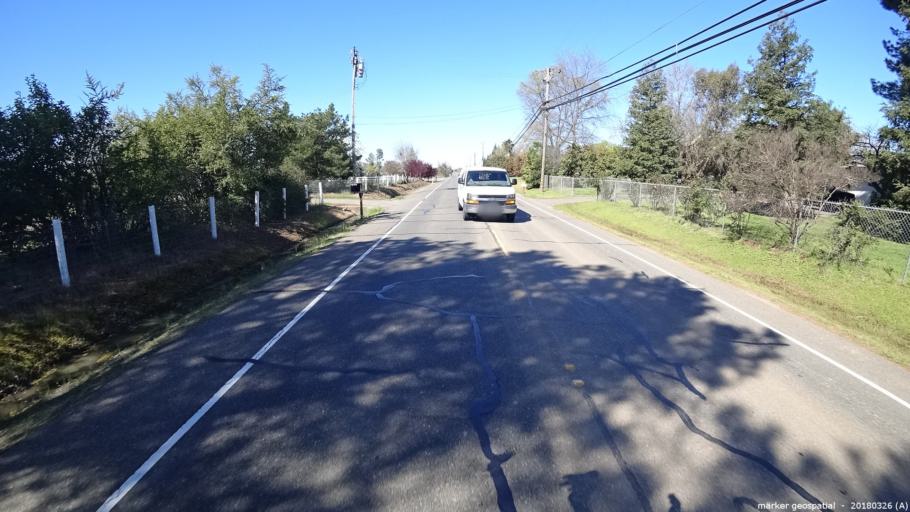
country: US
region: California
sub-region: Sacramento County
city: Wilton
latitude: 38.4527
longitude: -121.2933
